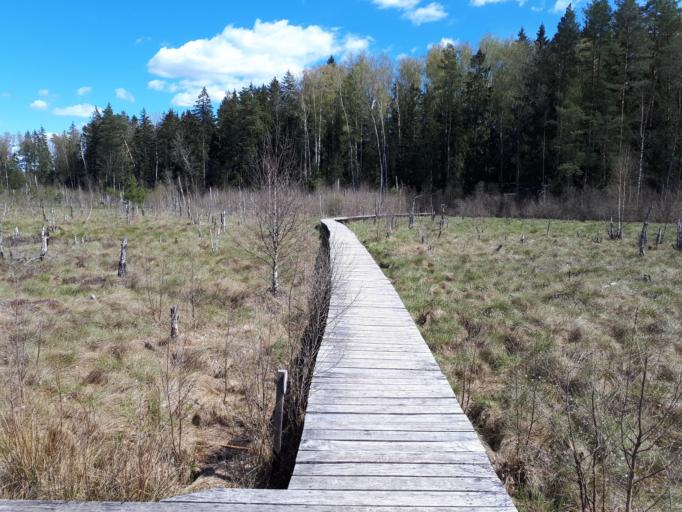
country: LT
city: Ramuciai
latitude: 54.8482
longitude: 24.0771
